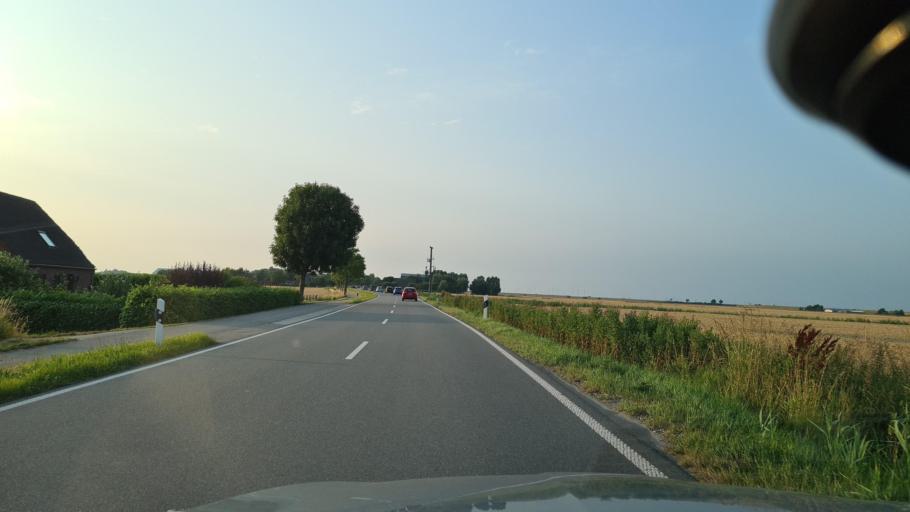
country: DE
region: Schleswig-Holstein
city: Elisabeth-Sophien-Koog
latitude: 54.5009
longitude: 8.9398
